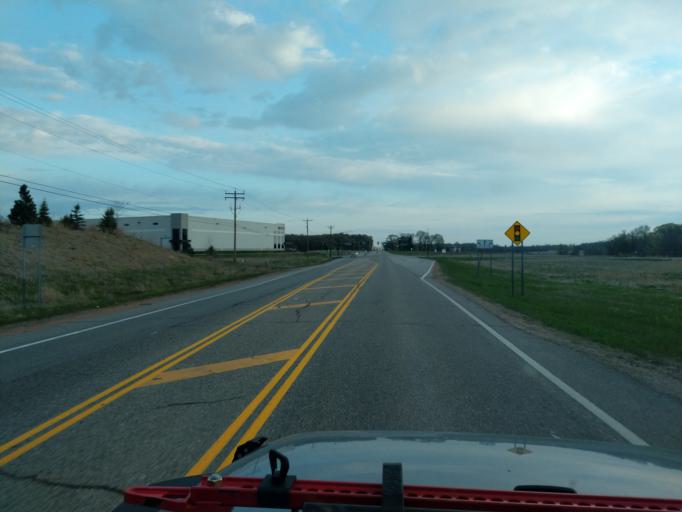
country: US
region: Minnesota
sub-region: Hennepin County
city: Rogers
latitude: 45.1805
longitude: -93.5226
